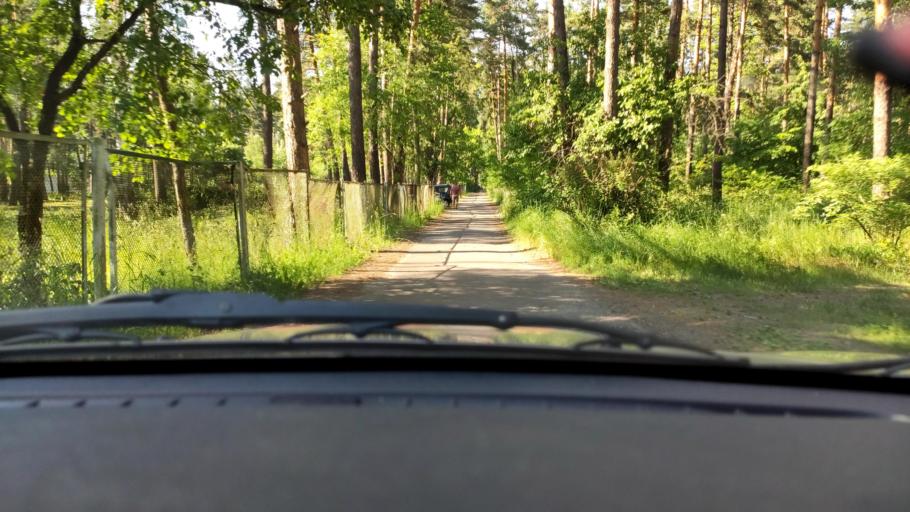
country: RU
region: Voronezj
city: Somovo
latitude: 51.7573
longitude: 39.3745
